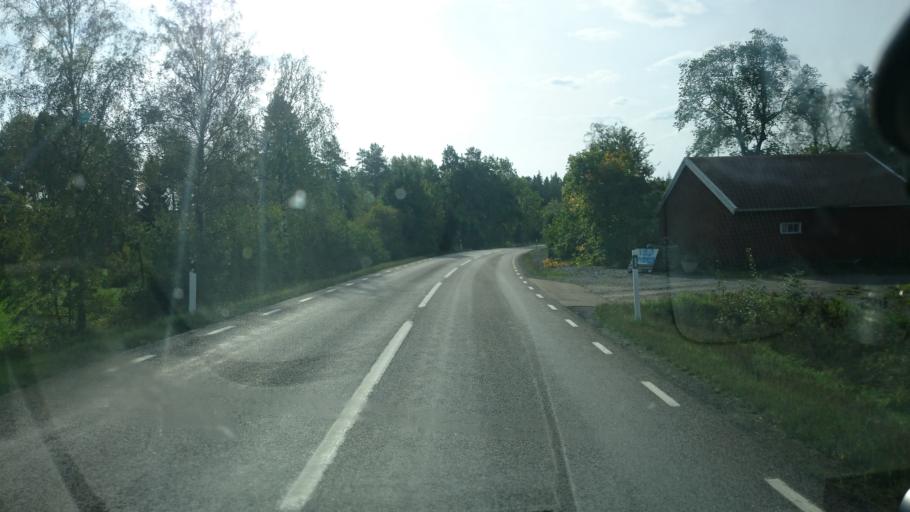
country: SE
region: Vaestra Goetaland
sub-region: Vanersborgs Kommun
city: Vargon
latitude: 58.2280
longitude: 12.4242
